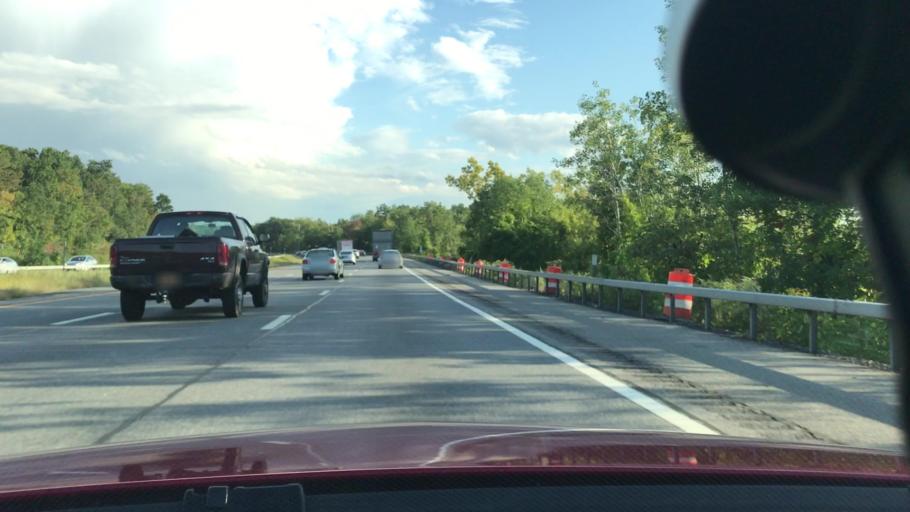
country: US
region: New York
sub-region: Albany County
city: Cohoes
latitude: 42.7972
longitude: -73.7648
